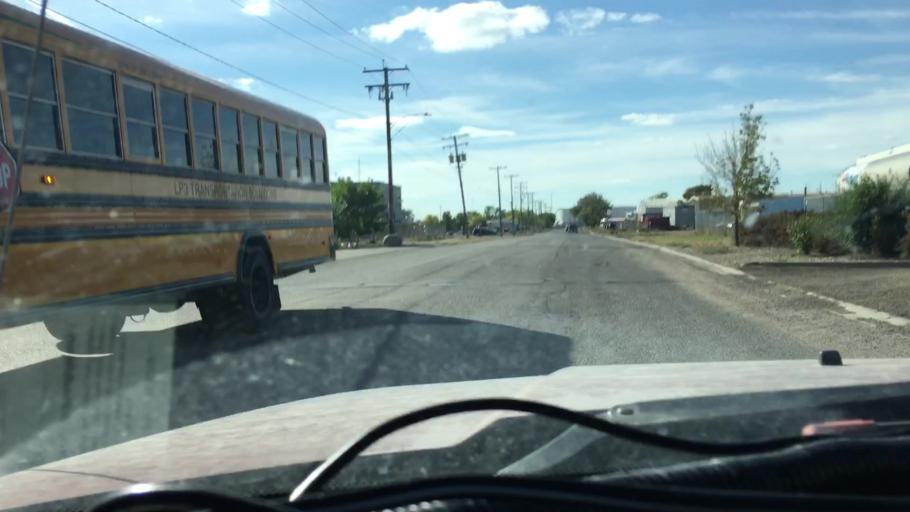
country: CA
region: Saskatchewan
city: Regina
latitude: 50.4788
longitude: -104.5656
